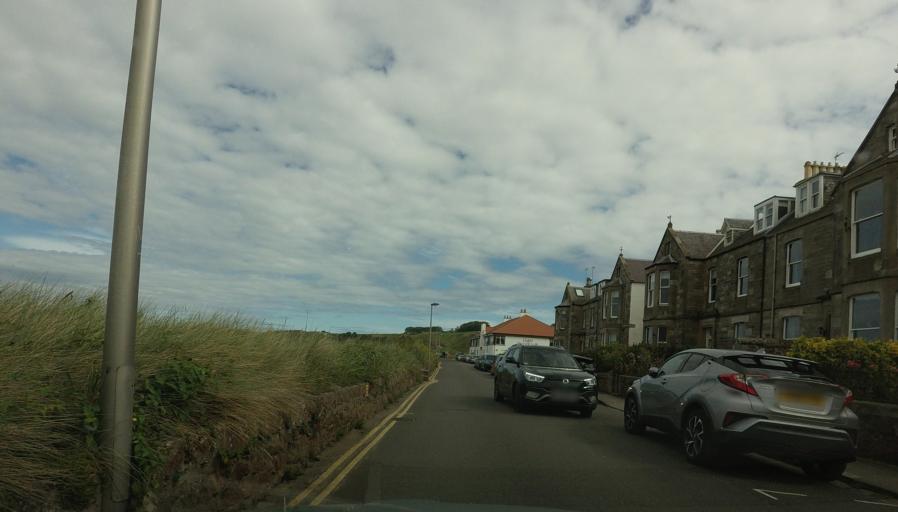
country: GB
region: Scotland
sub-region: East Lothian
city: North Berwick
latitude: 56.0574
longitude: -2.7048
